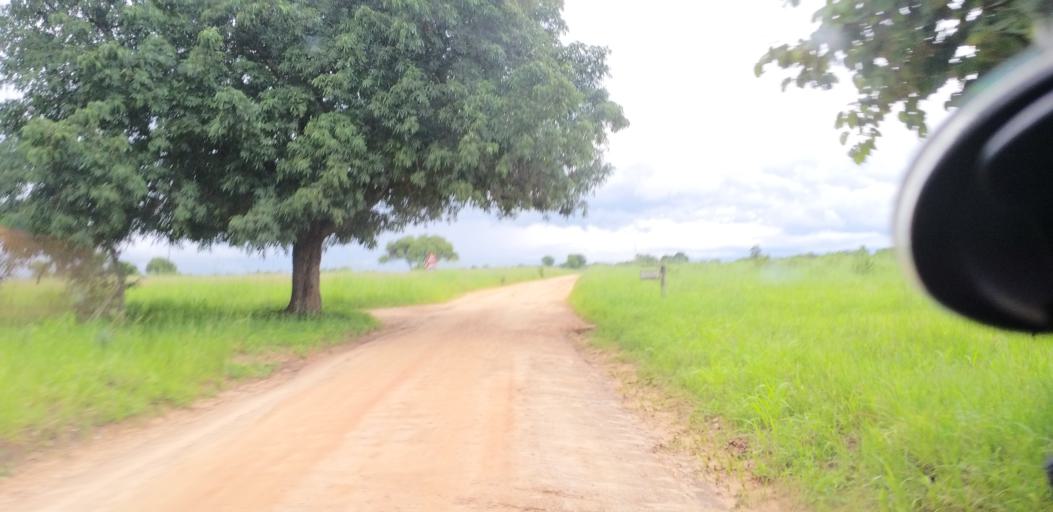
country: ZM
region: Lusaka
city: Chongwe
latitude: -15.1583
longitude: 28.4943
